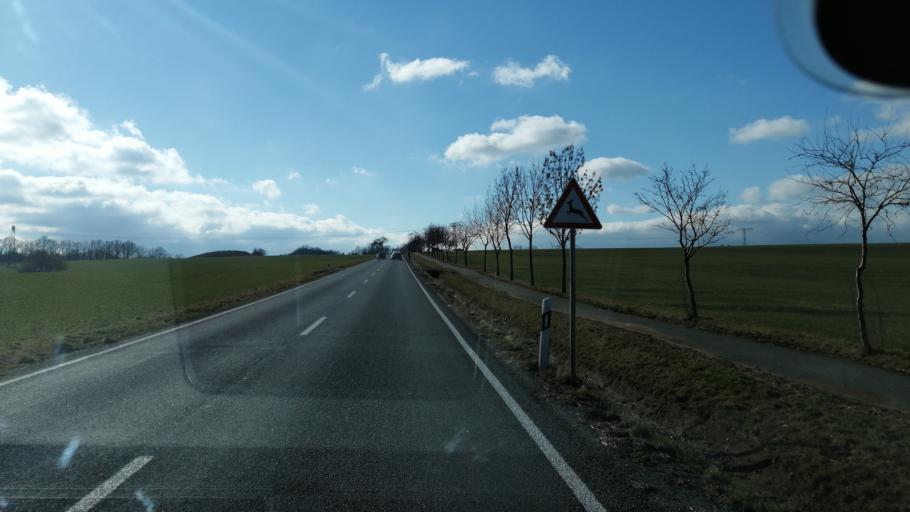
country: DE
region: Saxony
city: Lobau
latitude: 51.1428
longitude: 14.7061
